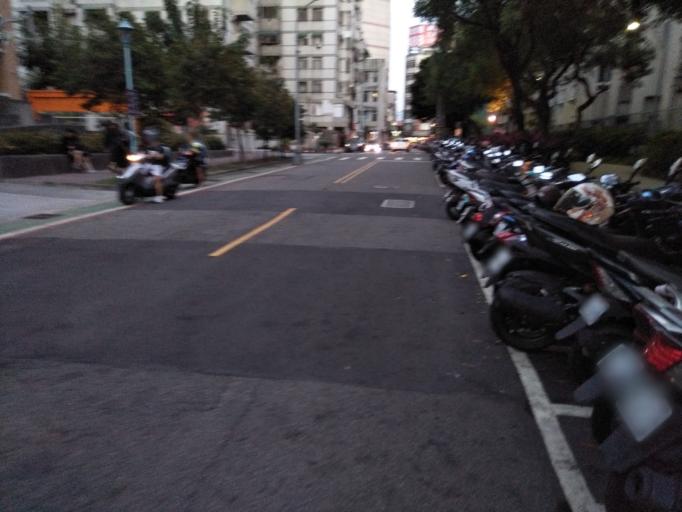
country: TW
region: Taiwan
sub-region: Taichung City
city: Taichung
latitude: 24.1520
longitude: 120.6835
